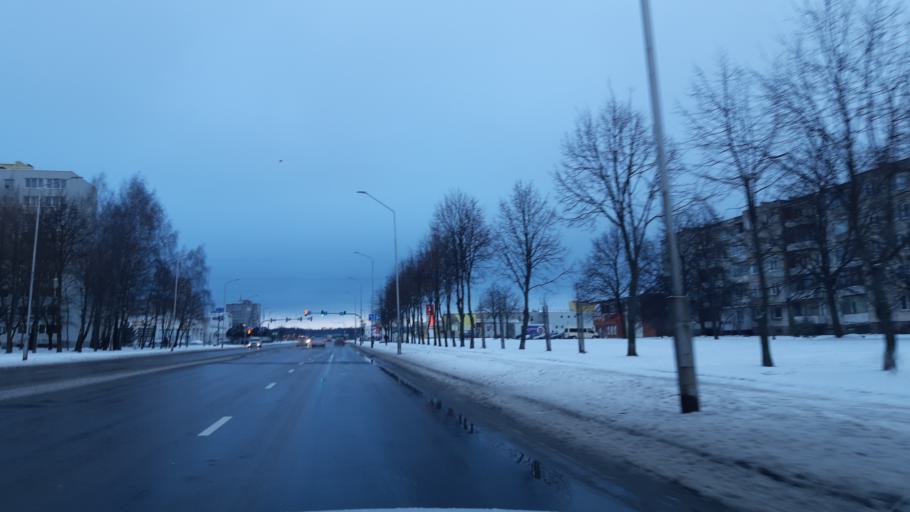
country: LT
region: Kauno apskritis
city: Dainava (Kaunas)
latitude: 54.9254
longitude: 23.9762
